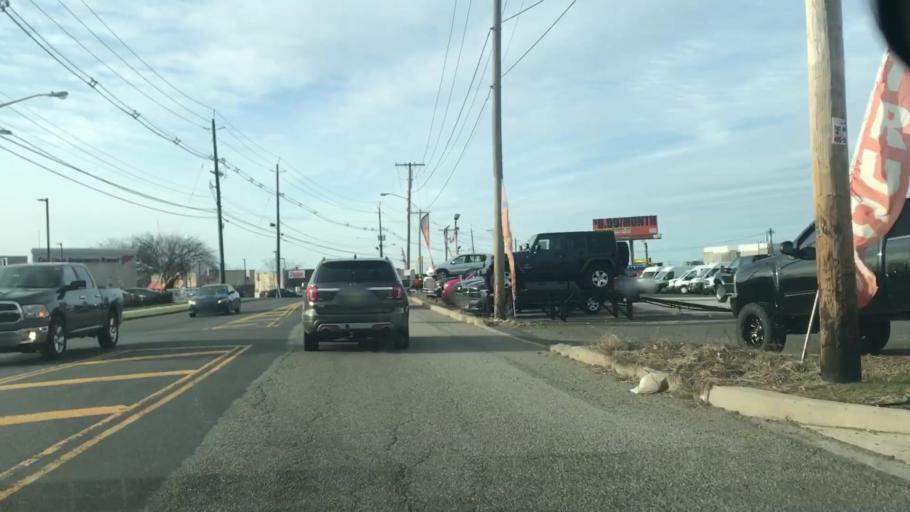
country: US
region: New Jersey
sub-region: Middlesex County
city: South River
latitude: 40.4615
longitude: -74.4013
